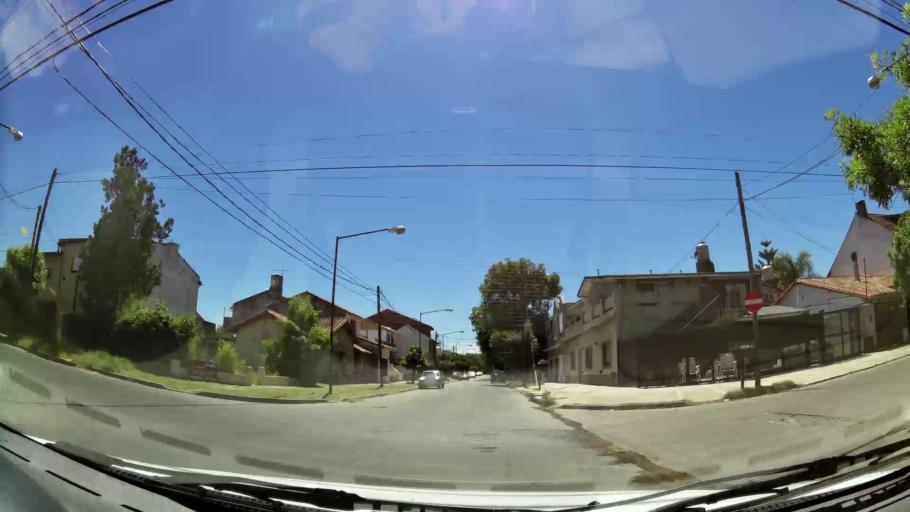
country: AR
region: Buenos Aires
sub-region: Partido de Vicente Lopez
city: Olivos
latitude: -34.5133
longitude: -58.5340
